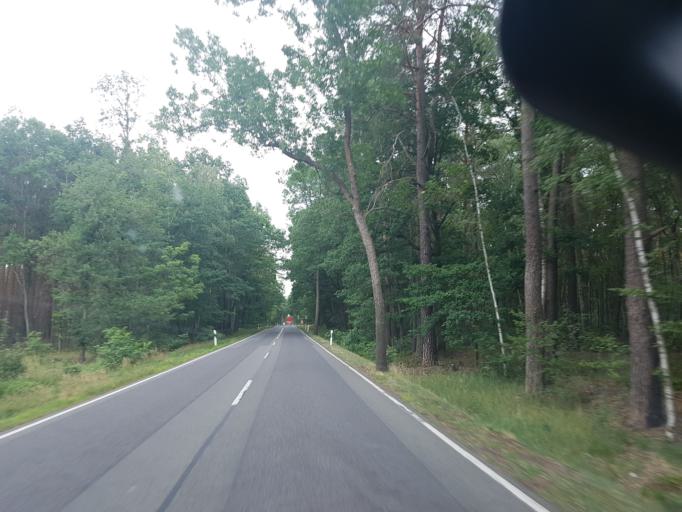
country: DE
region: Brandenburg
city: Lebusa
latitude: 51.8190
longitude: 13.4187
